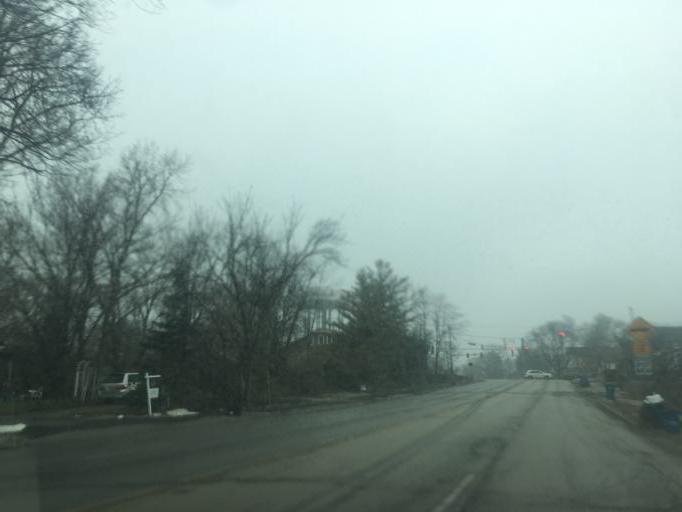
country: US
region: Illinois
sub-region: DuPage County
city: Downers Grove
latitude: 41.7865
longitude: -88.0089
